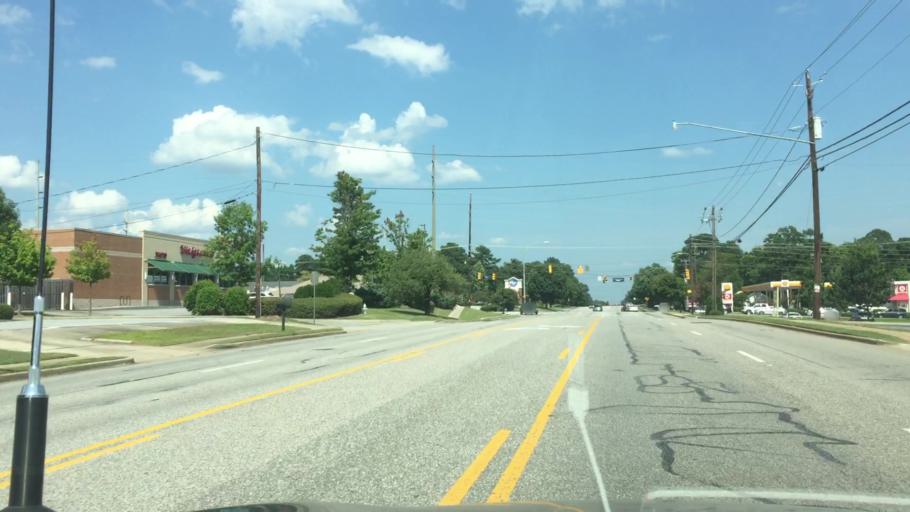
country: US
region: Alabama
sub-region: Lee County
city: Auburn
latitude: 32.6090
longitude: -85.4664
